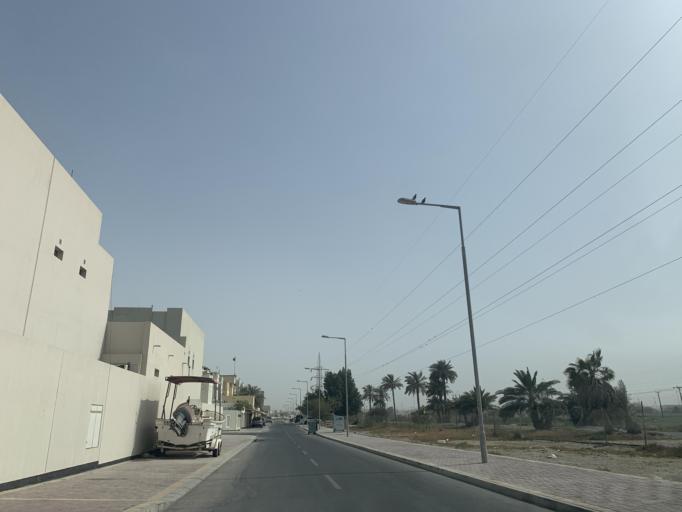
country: BH
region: Northern
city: Madinat `Isa
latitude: 26.1674
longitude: 50.5362
